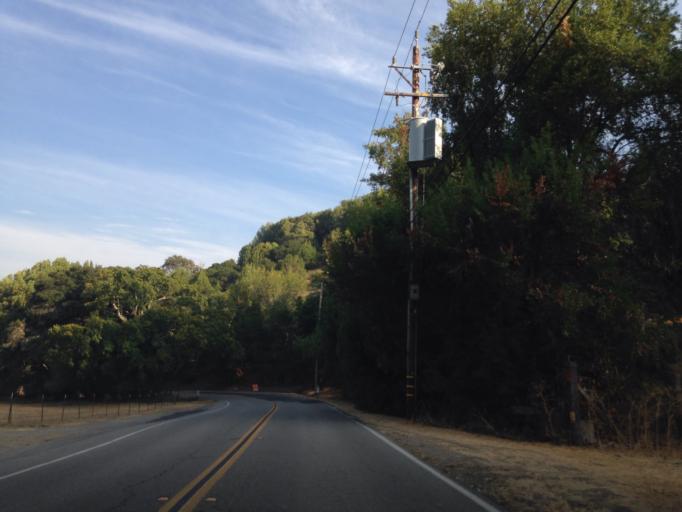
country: US
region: California
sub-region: Marin County
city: Lucas Valley-Marinwood
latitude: 38.0393
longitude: -122.6040
